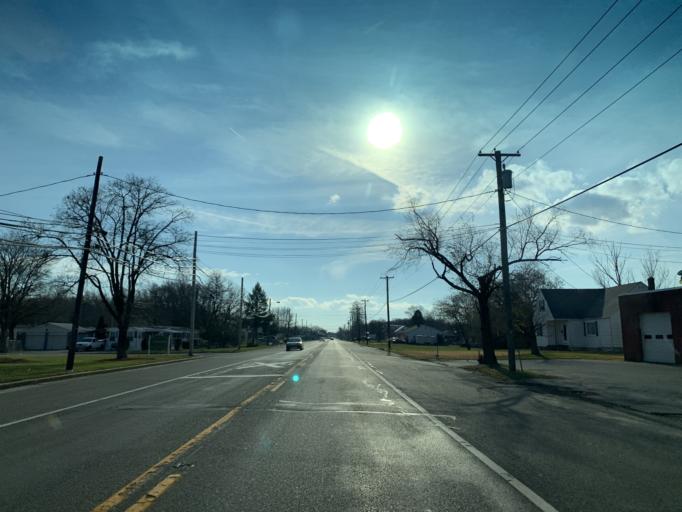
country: US
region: New Jersey
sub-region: Salem County
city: Penns Grove
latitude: 39.7402
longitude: -75.4564
